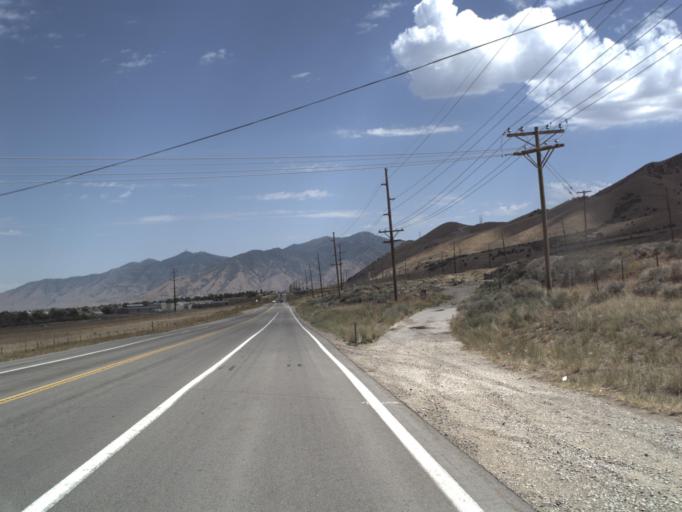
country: US
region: Utah
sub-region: Tooele County
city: Tooele
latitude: 40.4829
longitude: -112.3417
